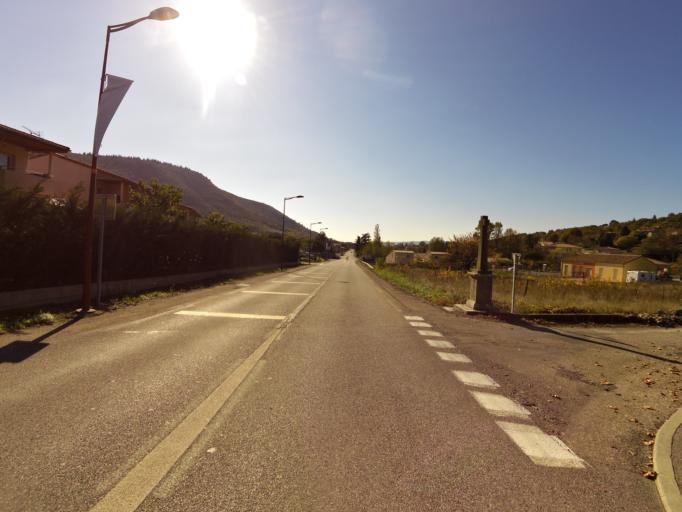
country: FR
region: Rhone-Alpes
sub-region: Departement de l'Ardeche
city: Vesseaux
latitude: 44.6503
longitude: 4.4415
